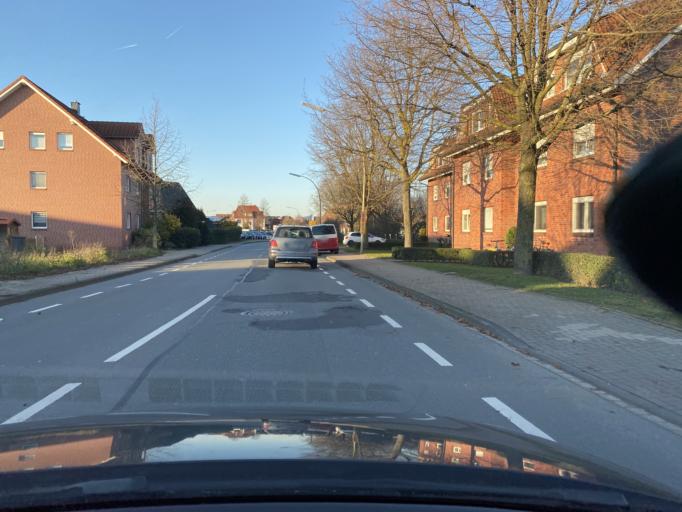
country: DE
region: North Rhine-Westphalia
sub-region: Regierungsbezirk Munster
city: Ascheberg
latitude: 51.7422
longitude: 7.6636
